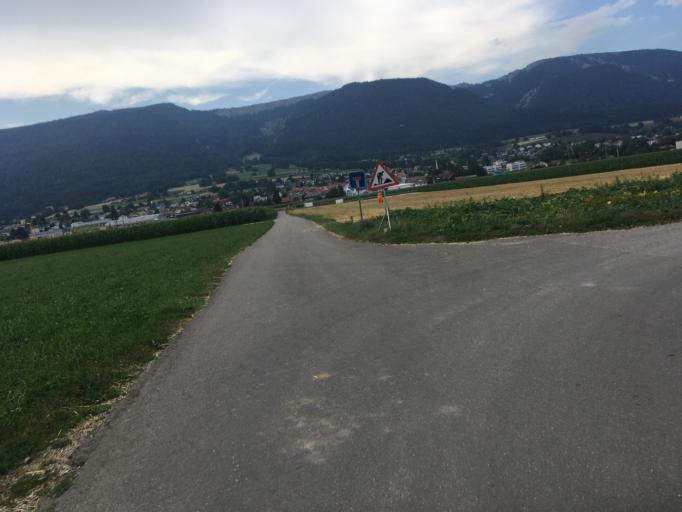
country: CH
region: Solothurn
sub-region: Bezirk Lebern
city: Bettlach
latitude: 47.1909
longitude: 7.4219
